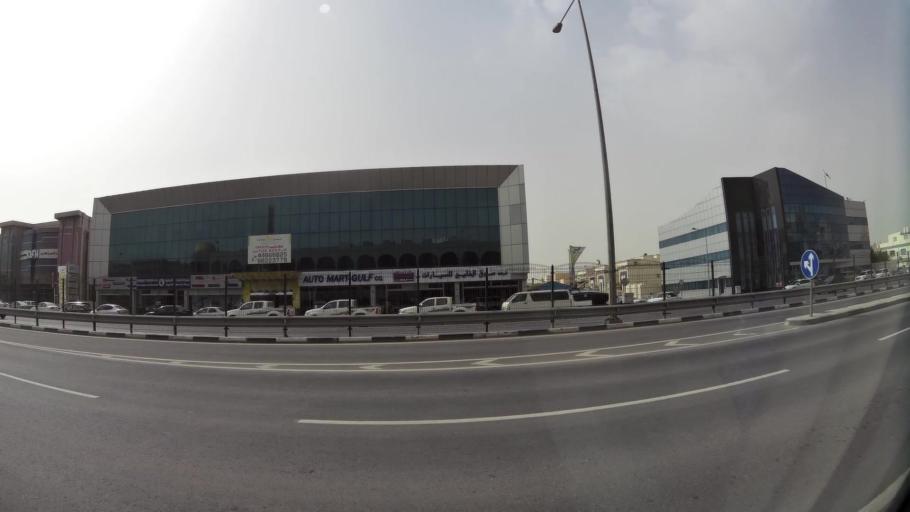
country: QA
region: Baladiyat ad Dawhah
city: Doha
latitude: 25.2630
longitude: 51.5348
